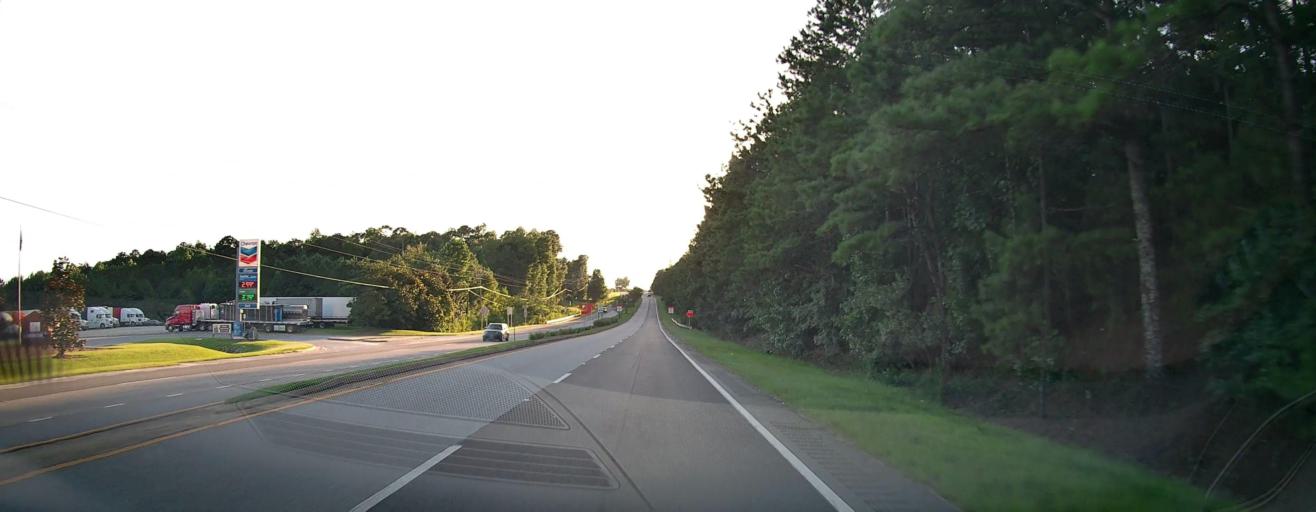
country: US
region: Georgia
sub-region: Muscogee County
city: Columbus
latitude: 32.5384
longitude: -84.8466
